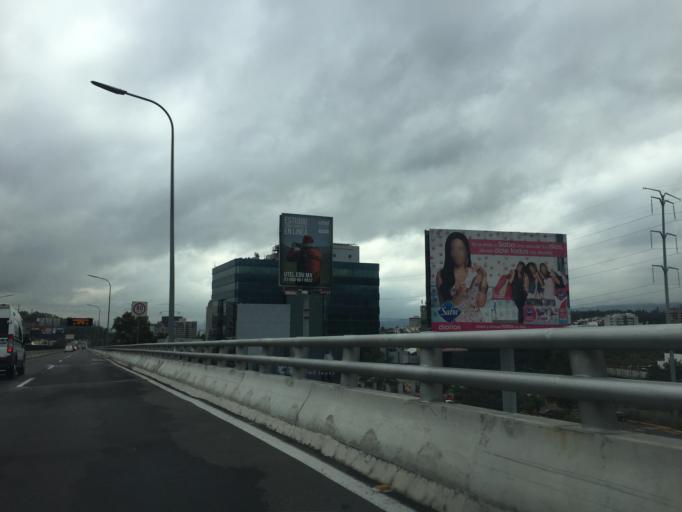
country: MX
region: Mexico City
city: Magdalena Contreras
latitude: 19.3068
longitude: -99.2123
